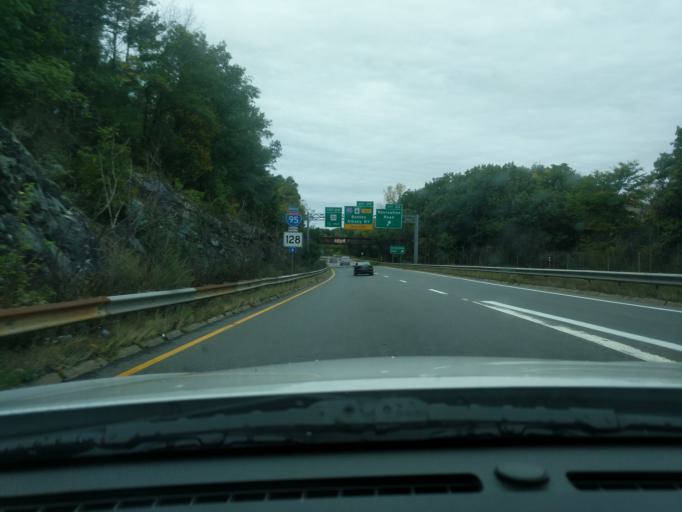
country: US
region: Massachusetts
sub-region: Middlesex County
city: Waltham
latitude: 42.3352
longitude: -71.2561
